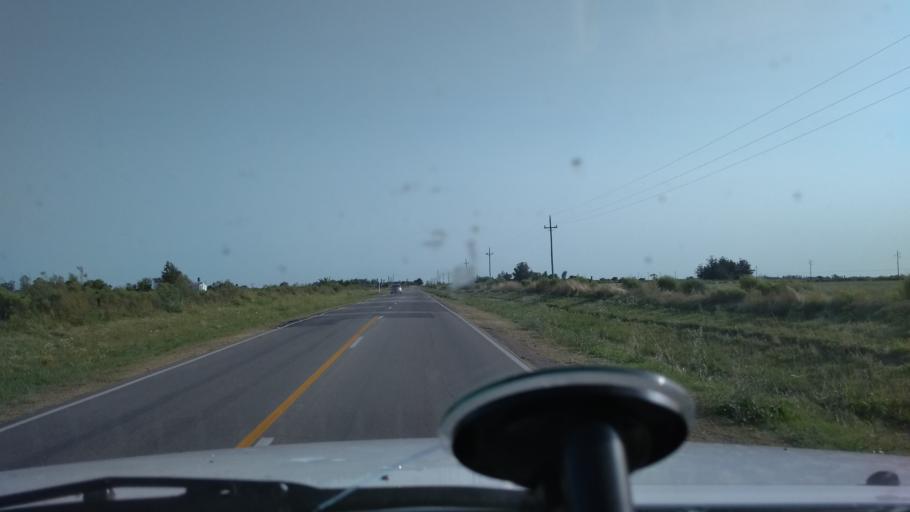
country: UY
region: Canelones
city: Santa Rosa
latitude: -34.5131
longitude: -56.0542
